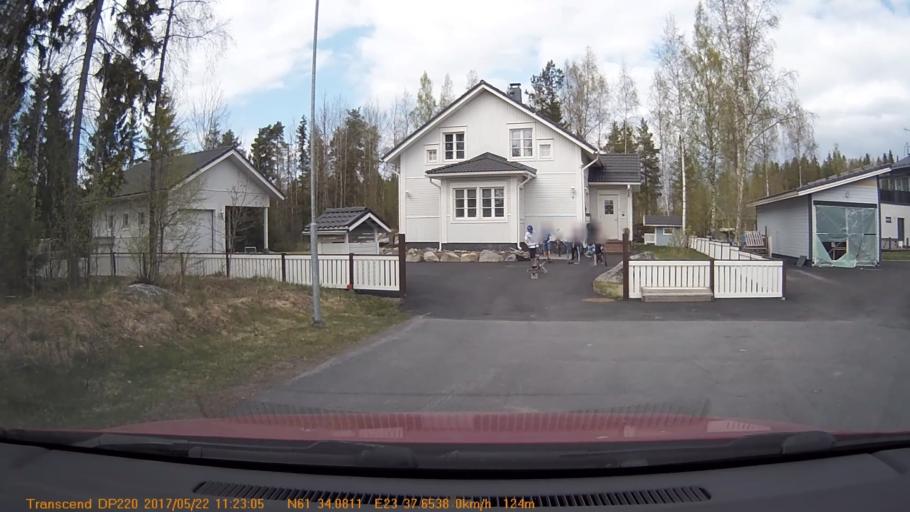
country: FI
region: Pirkanmaa
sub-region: Tampere
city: Yloejaervi
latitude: 61.5680
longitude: 23.6276
